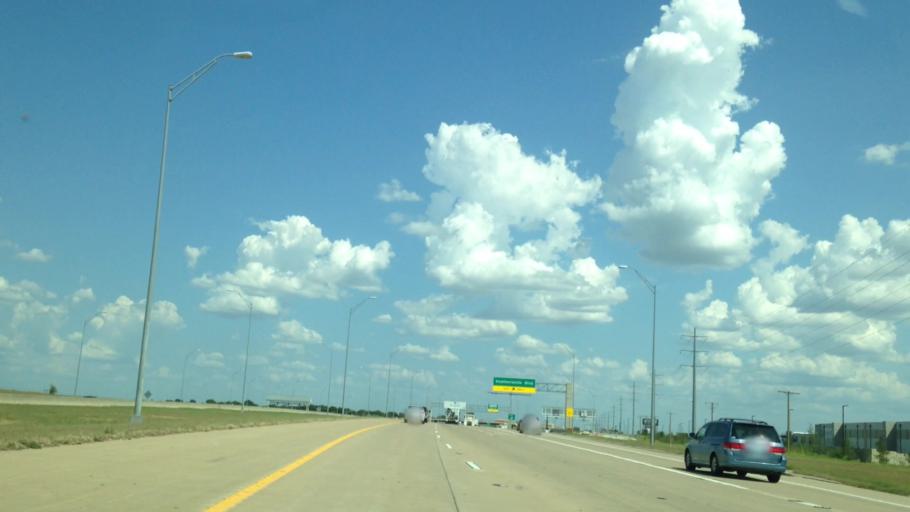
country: US
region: Texas
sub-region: Travis County
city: Windemere
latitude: 30.4877
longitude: -97.6203
